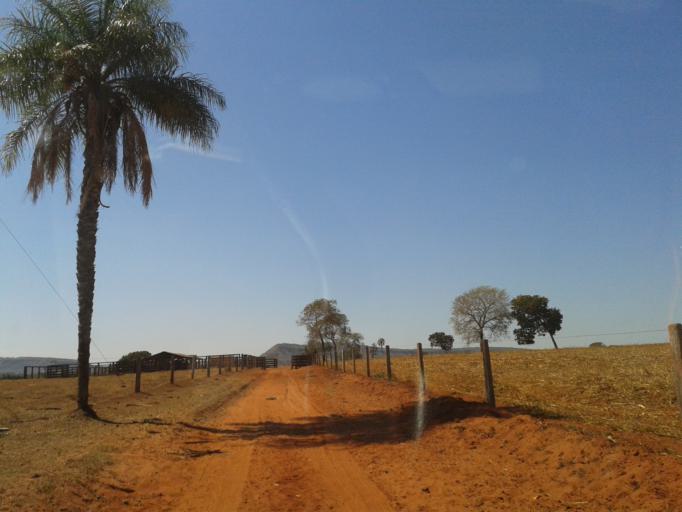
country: BR
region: Minas Gerais
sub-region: Santa Vitoria
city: Santa Vitoria
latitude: -19.0856
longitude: -50.0746
